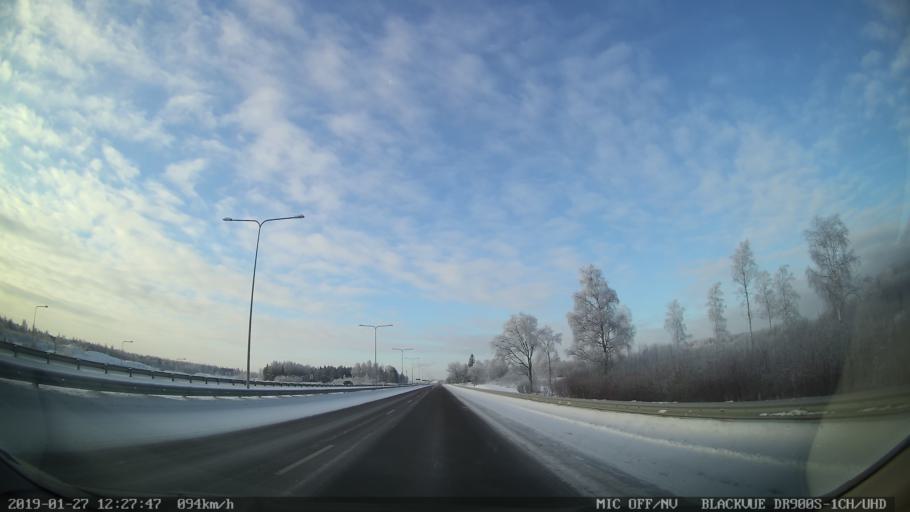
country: EE
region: Harju
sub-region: Maardu linn
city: Maardu
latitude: 59.4520
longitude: 25.0339
